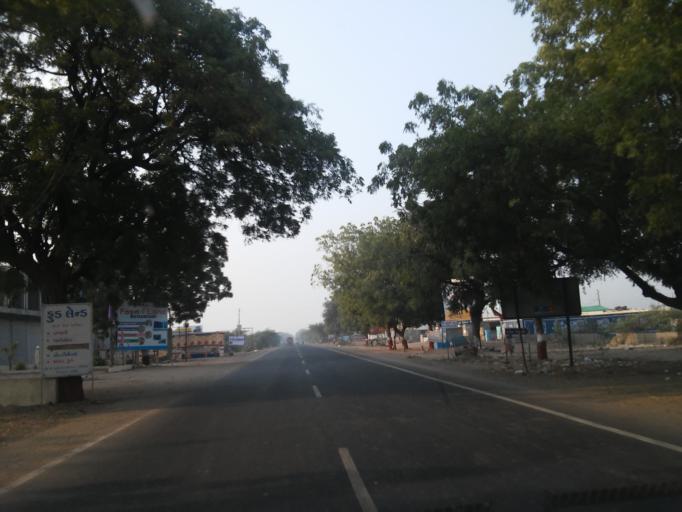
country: IN
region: Gujarat
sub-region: Kachchh
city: Mandvi
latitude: 22.8977
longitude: 69.4111
